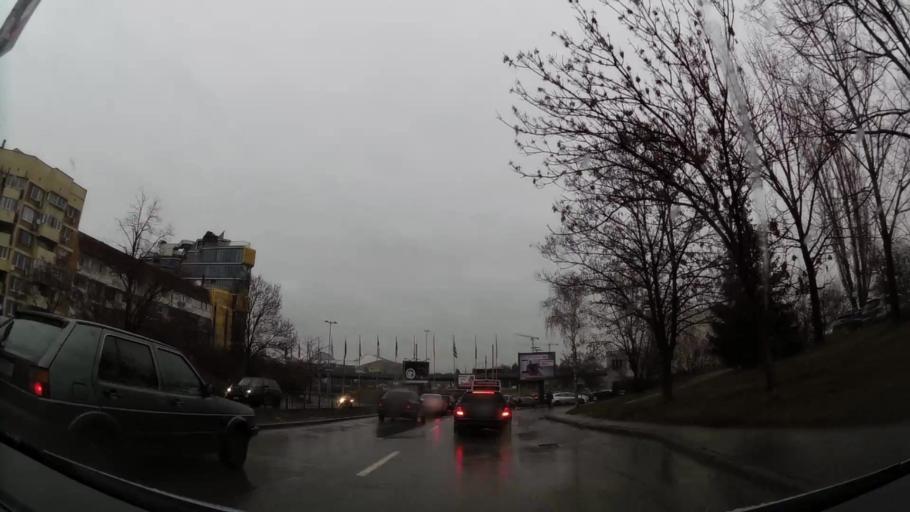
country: BG
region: Sofia-Capital
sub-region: Stolichna Obshtina
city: Sofia
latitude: 42.6679
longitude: 23.3665
